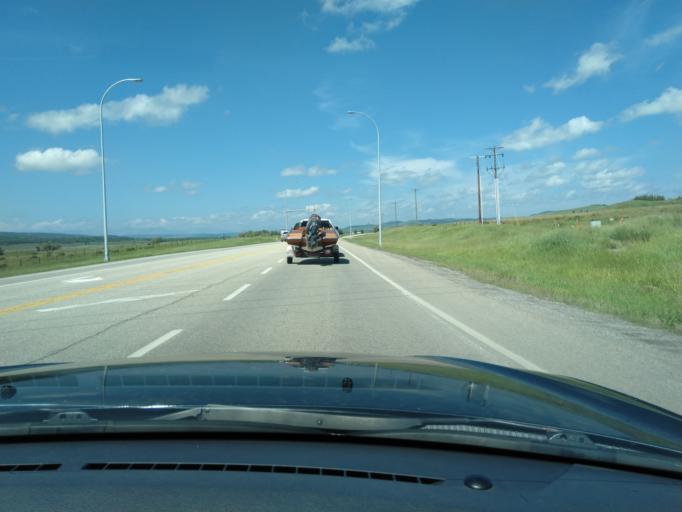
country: CA
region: Alberta
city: Cochrane
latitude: 51.2065
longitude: -114.5130
